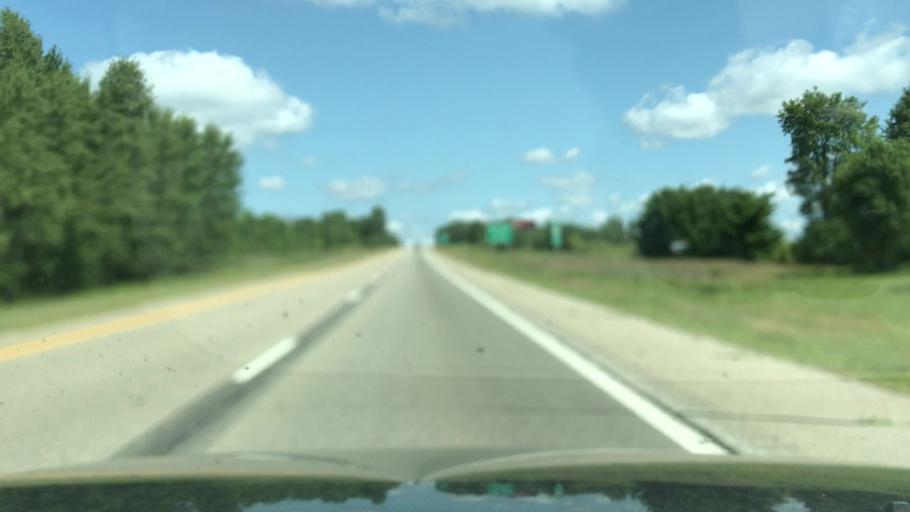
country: US
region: Michigan
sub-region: Mecosta County
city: Big Rapids
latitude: 43.7183
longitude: -85.5308
